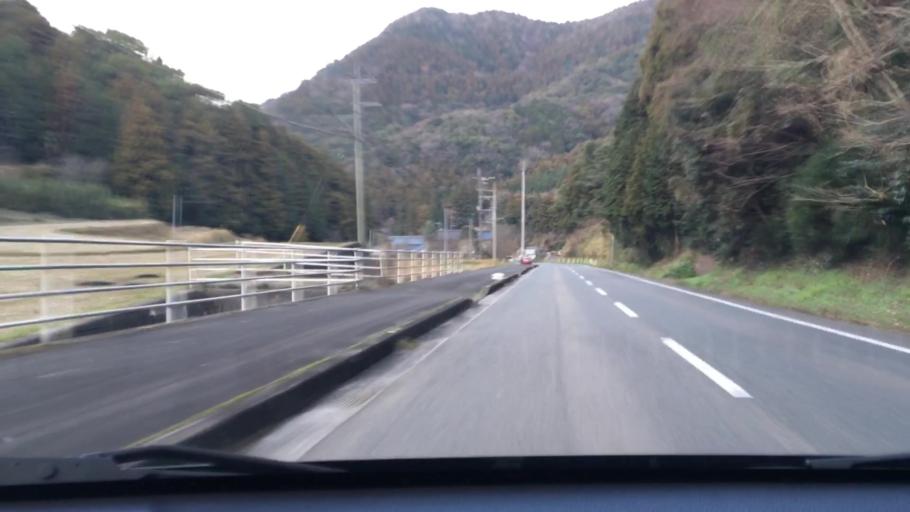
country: JP
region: Oita
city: Bungo-Takada-shi
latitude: 33.4793
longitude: 131.3863
